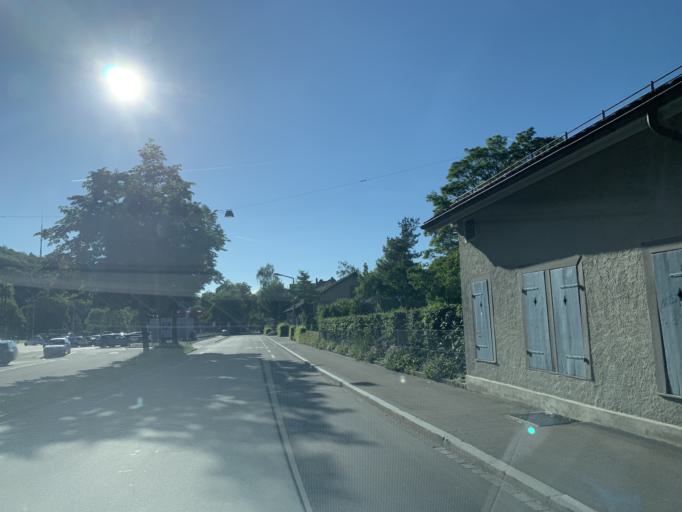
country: CH
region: Zurich
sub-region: Bezirk Winterthur
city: Stadt Winterthur (Kreis 1) / Neuwiesen
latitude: 47.5021
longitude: 8.7181
